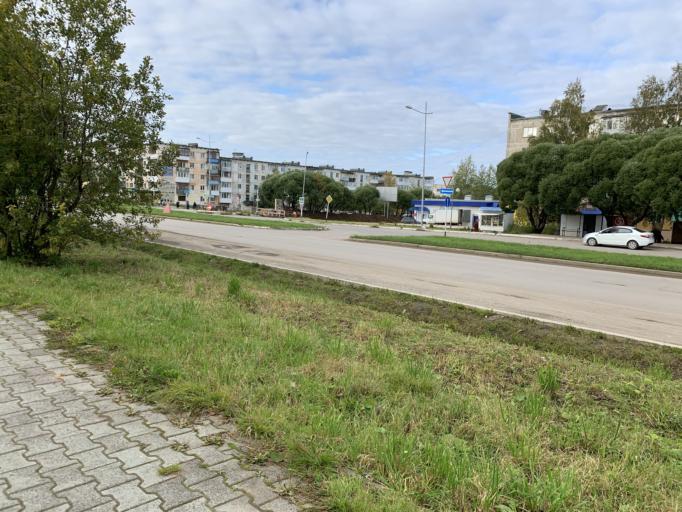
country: RU
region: Perm
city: Gubakha
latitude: 58.8300
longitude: 57.5585
